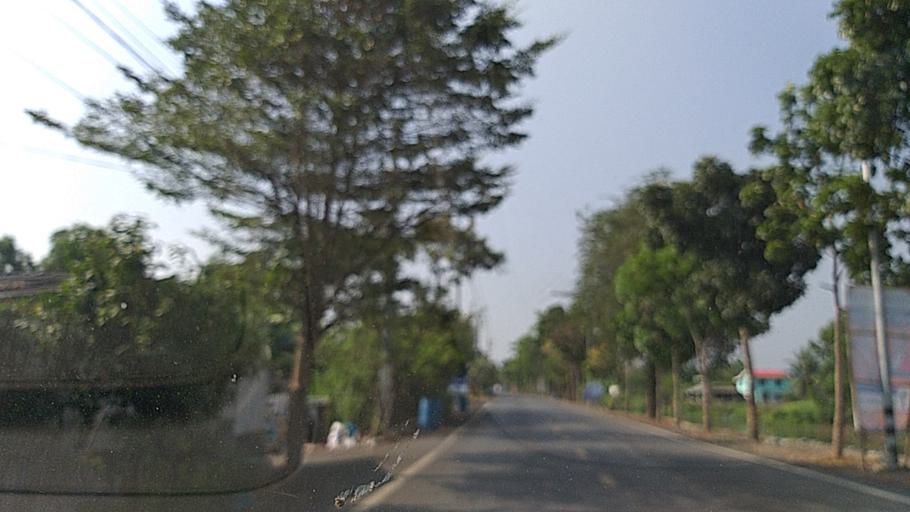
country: TH
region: Pathum Thani
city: Thanyaburi
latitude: 13.9917
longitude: 100.7061
